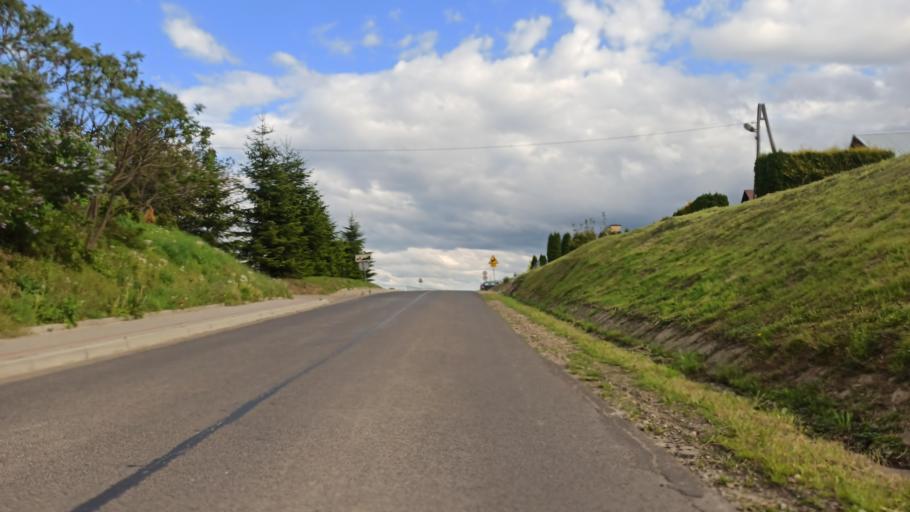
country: PL
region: Subcarpathian Voivodeship
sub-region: Powiat jaroslawski
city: Sosnica
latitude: 49.9179
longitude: 22.8586
